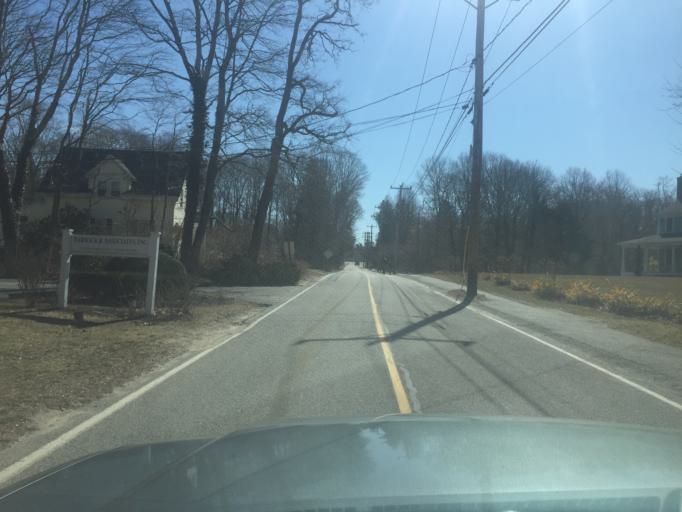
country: US
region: Massachusetts
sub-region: Barnstable County
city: North Falmouth
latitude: 41.6490
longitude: -70.6165
